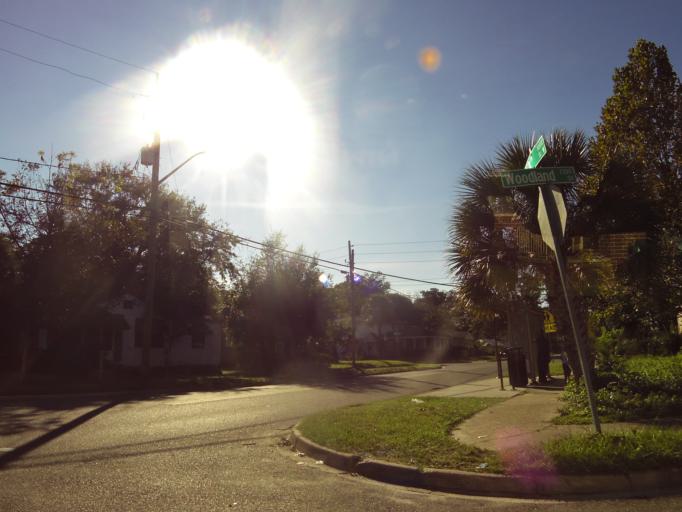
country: US
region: Florida
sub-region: Duval County
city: Jacksonville
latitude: 30.3514
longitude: -81.6711
